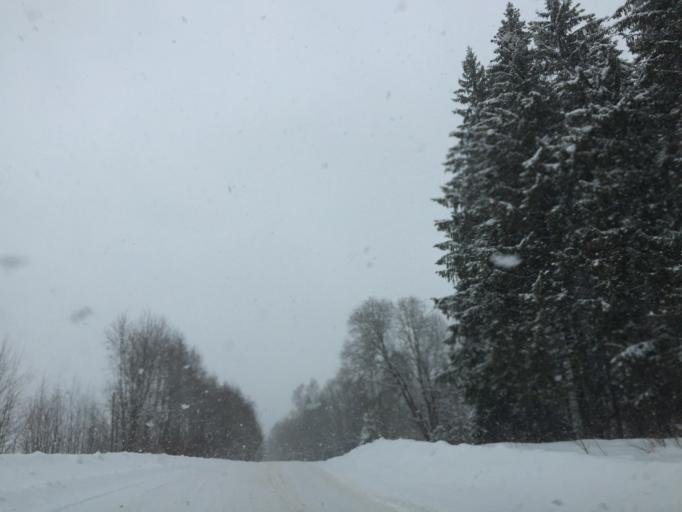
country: LV
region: Amatas Novads
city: Drabesi
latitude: 57.0759
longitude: 25.3414
